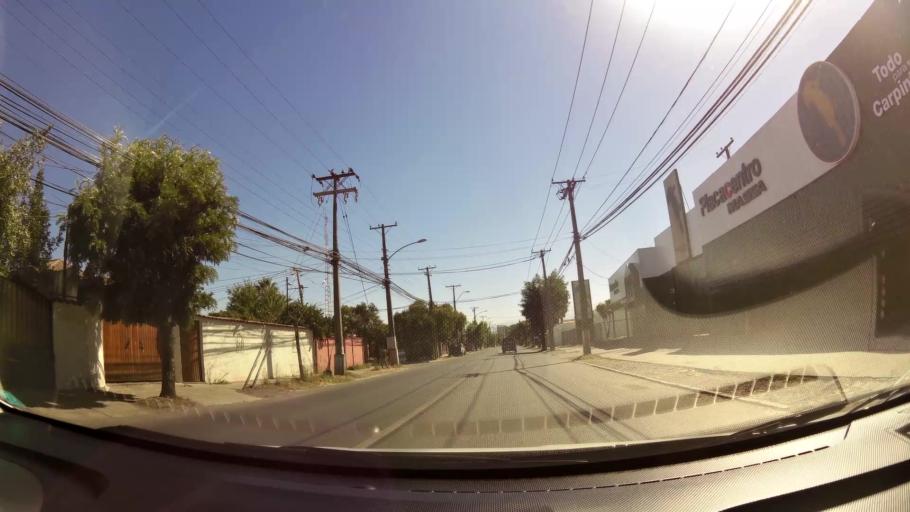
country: CL
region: O'Higgins
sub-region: Provincia de Cachapoal
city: Rancagua
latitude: -34.1801
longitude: -70.7454
